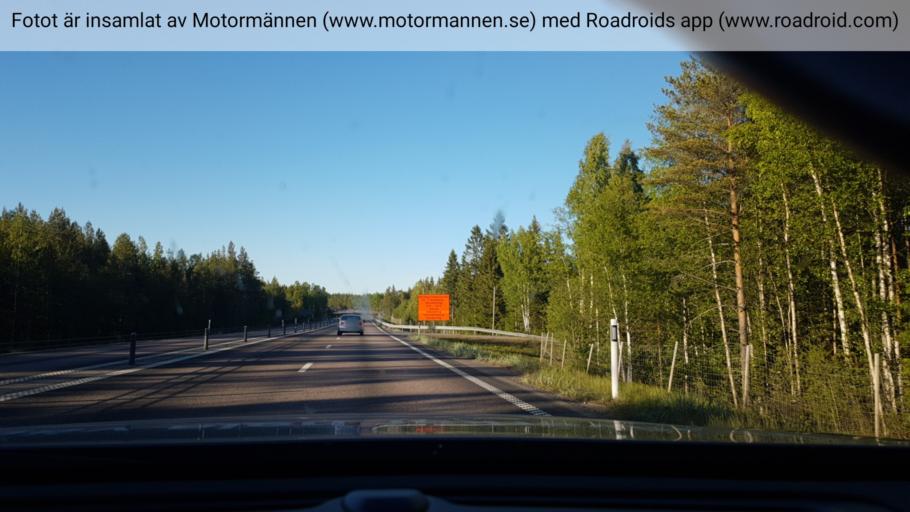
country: SE
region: Vaesternorrland
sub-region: OErnskoeldsviks Kommun
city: Husum
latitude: 63.4683
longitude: 19.2743
